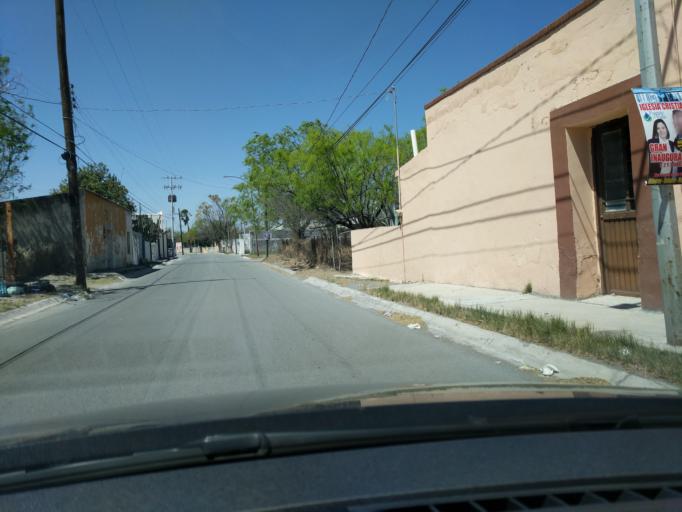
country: MX
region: Nuevo Leon
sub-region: Apodaca
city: Artemio Trevino
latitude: 25.8130
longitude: -100.1391
